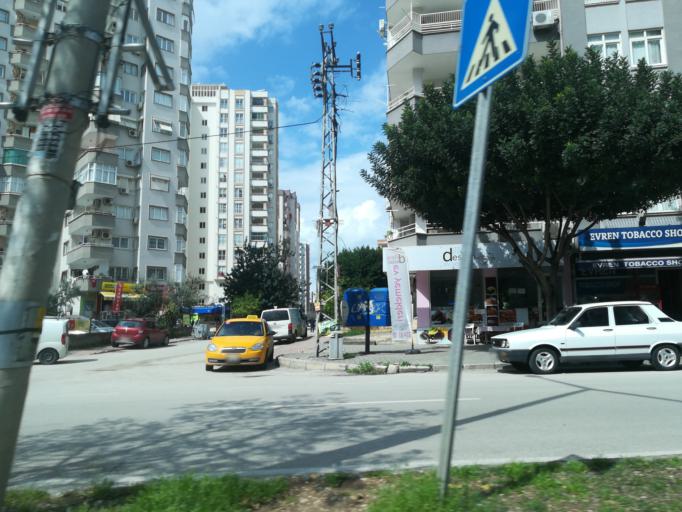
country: TR
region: Adana
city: Adana
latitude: 37.0381
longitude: 35.3003
